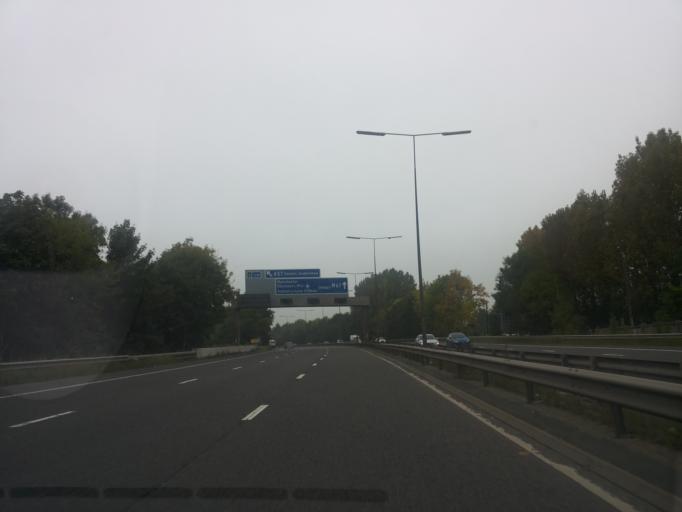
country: GB
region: England
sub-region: Borough of Tameside
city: Hyde
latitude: 53.4549
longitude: -2.0883
